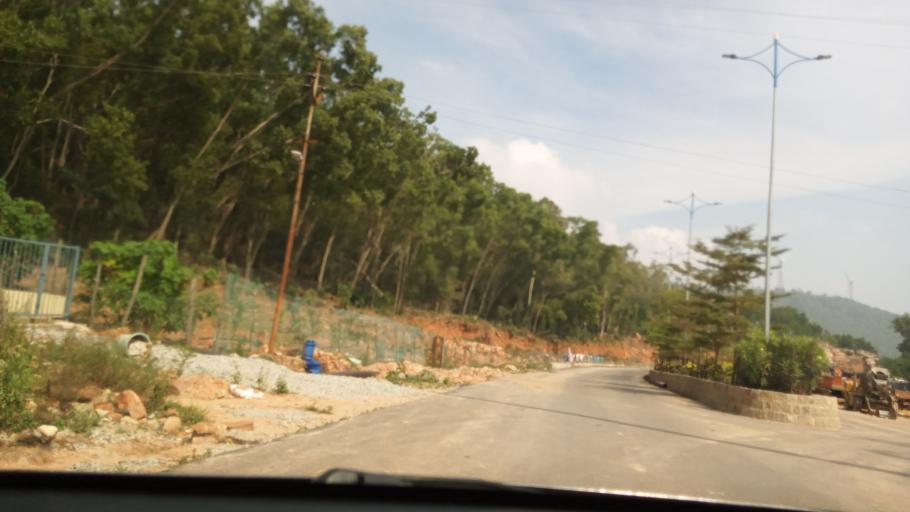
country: IN
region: Andhra Pradesh
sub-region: Chittoor
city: Tirumala
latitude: 13.6917
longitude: 79.3468
